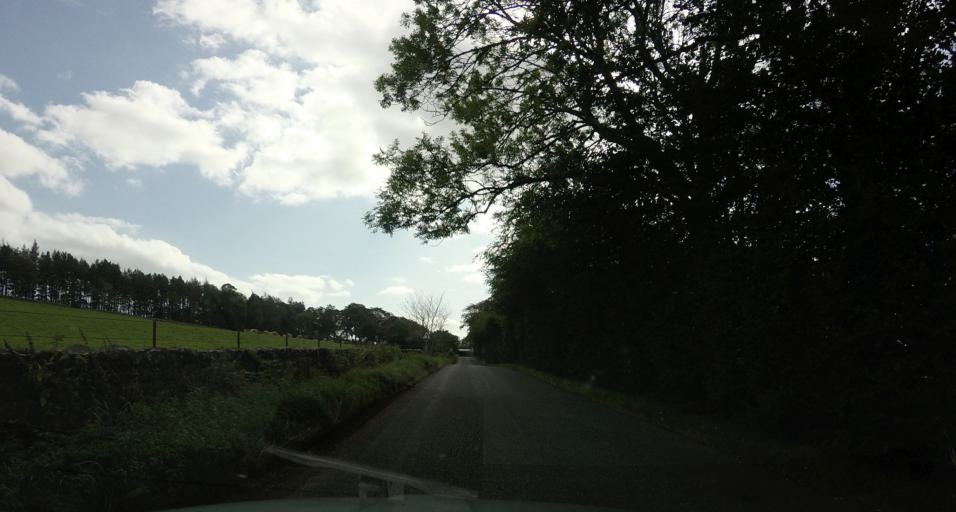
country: GB
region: Scotland
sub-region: Aberdeenshire
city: Kemnay
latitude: 57.2069
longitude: -2.4693
